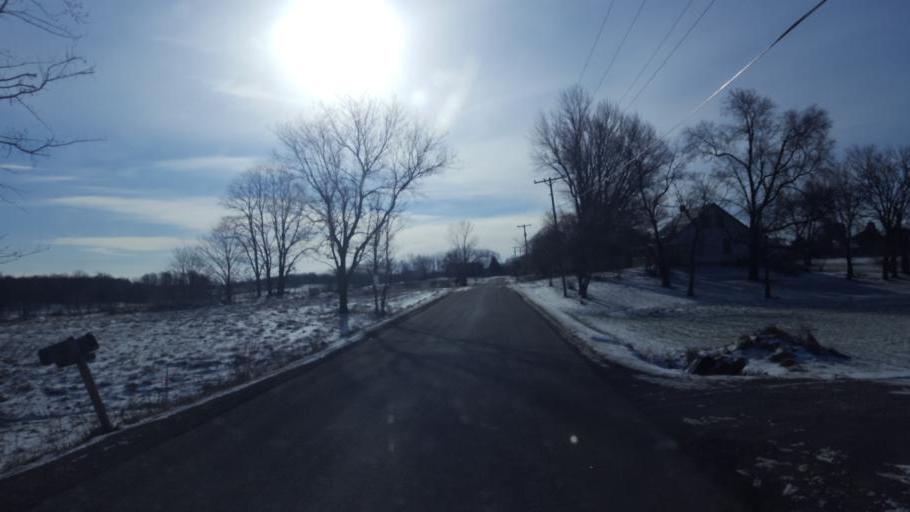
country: US
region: Ohio
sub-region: Morrow County
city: Mount Gilead
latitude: 40.5756
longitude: -82.7223
